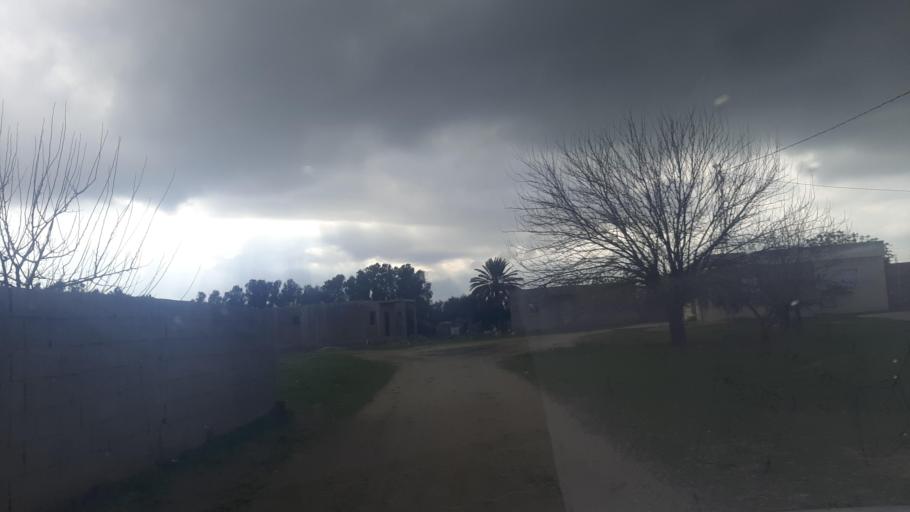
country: TN
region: Nabul
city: Manzil Bu Zalafah
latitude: 36.7354
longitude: 10.5247
